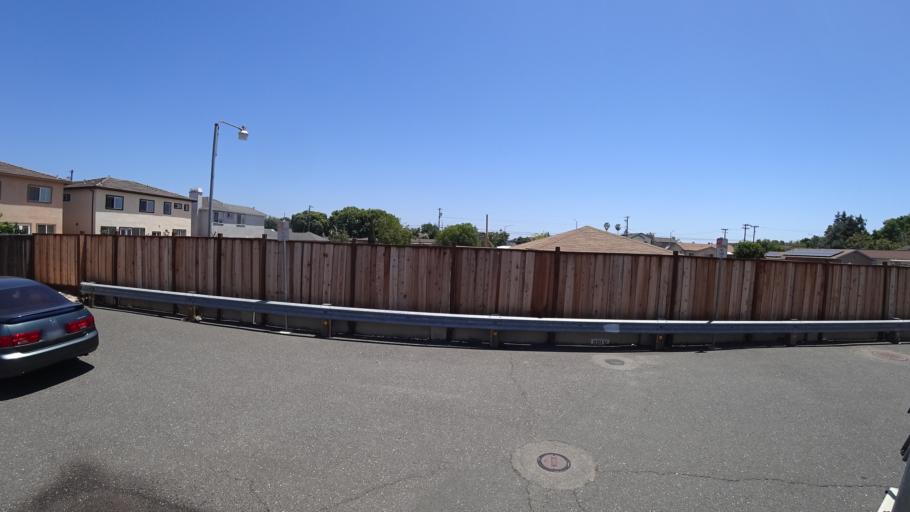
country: US
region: California
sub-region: Alameda County
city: Hayward
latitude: 37.6286
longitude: -122.0592
